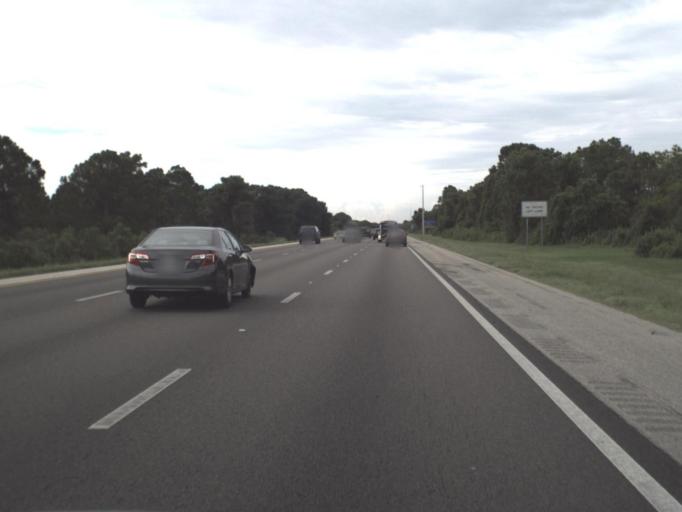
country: US
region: Florida
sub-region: Sarasota County
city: The Meadows
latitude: 27.3753
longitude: -82.4469
